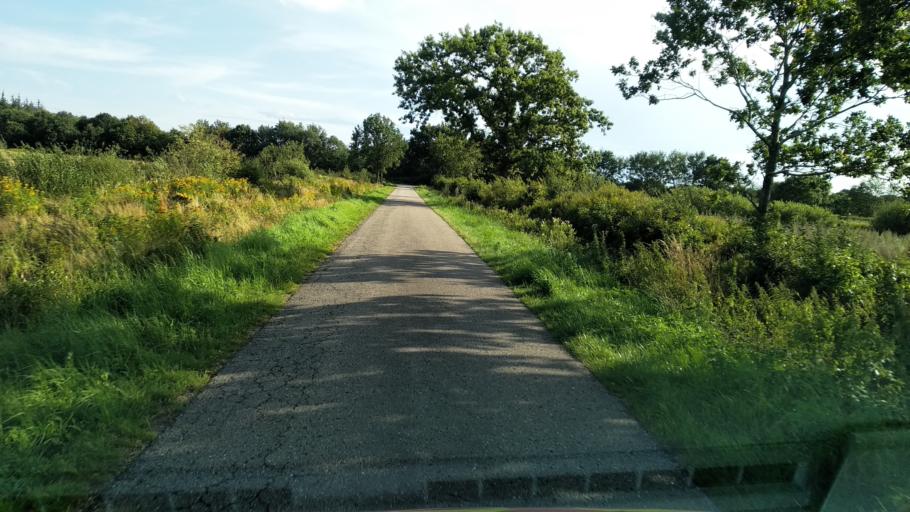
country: DE
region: Schleswig-Holstein
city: Gross Rheide
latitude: 54.4285
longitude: 9.4283
